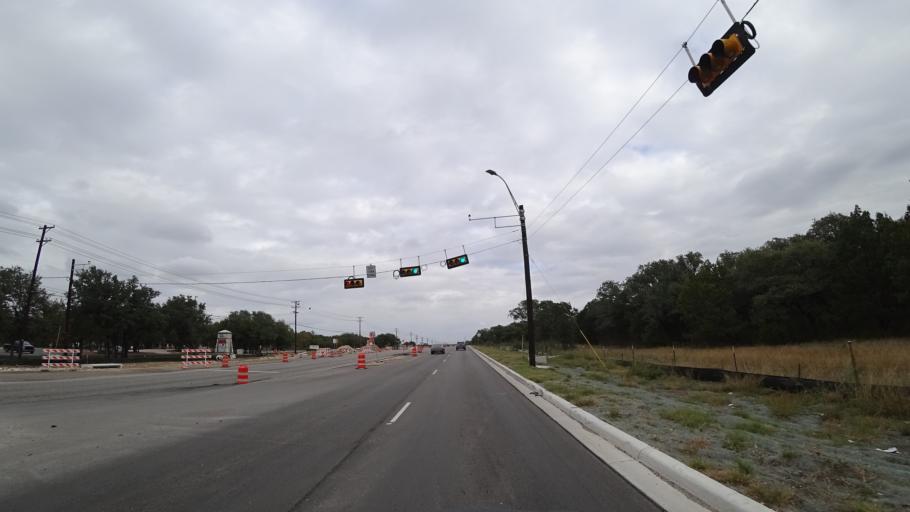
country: US
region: Texas
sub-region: Williamson County
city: Brushy Creek
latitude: 30.5092
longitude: -97.7123
